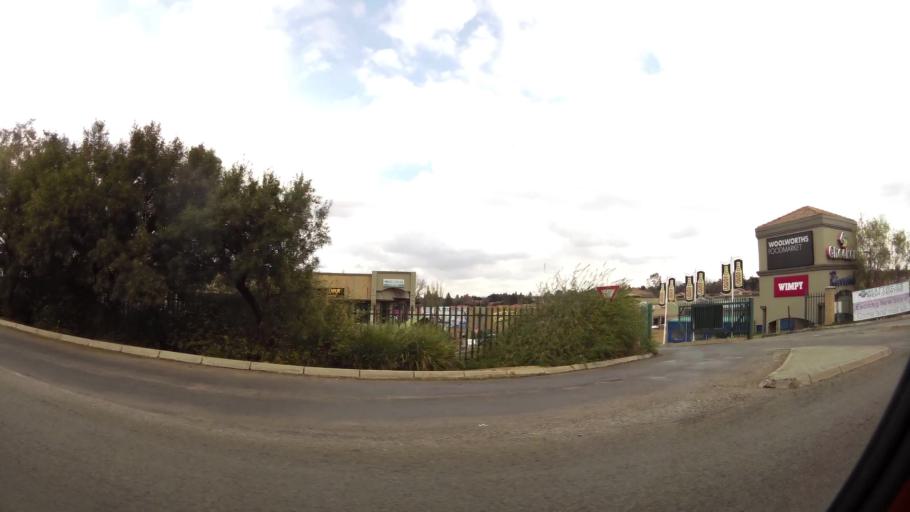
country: ZA
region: Gauteng
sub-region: Sedibeng District Municipality
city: Vanderbijlpark
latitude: -26.7339
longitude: 27.8406
